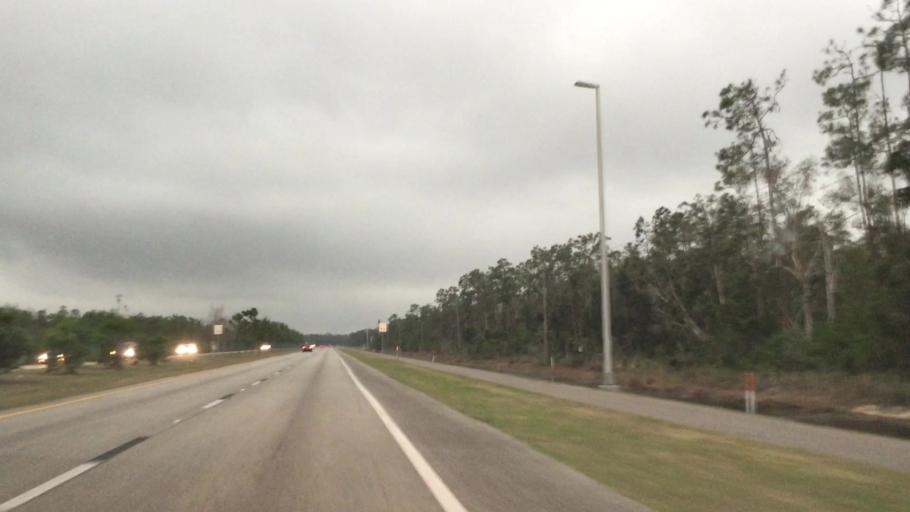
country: US
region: Florida
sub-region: Lee County
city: Villas
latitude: 26.5699
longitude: -81.8283
